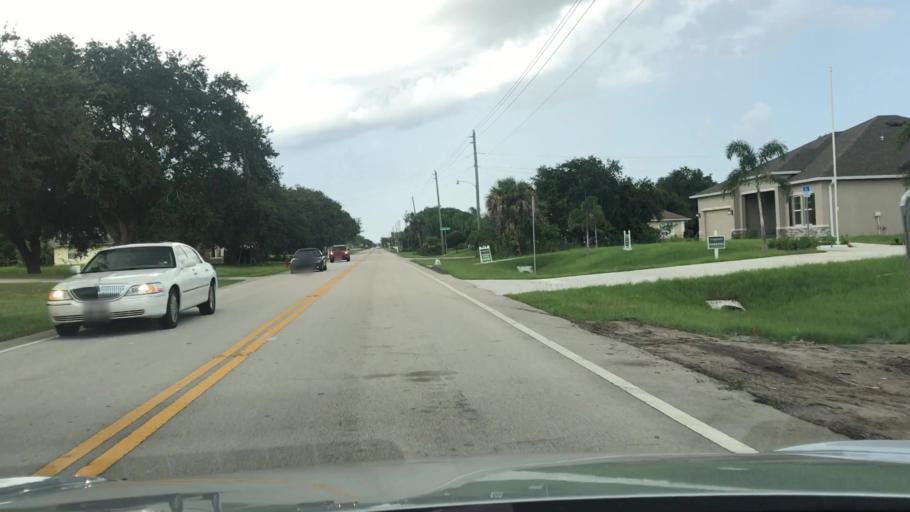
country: US
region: Florida
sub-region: Indian River County
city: Sebastian
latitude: 27.7868
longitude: -80.4984
